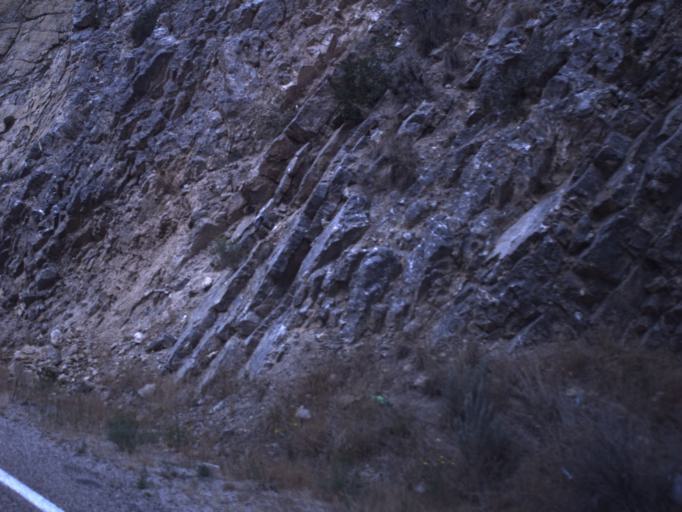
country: US
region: Utah
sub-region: Rich County
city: Randolph
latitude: 41.8246
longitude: -111.3006
